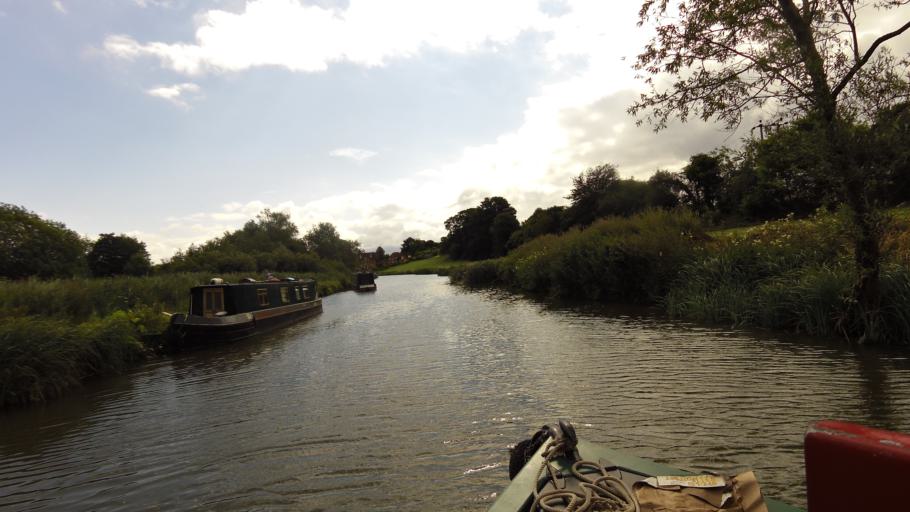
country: GB
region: England
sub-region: West Berkshire
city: Kintbury
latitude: 51.4021
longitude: -1.4563
